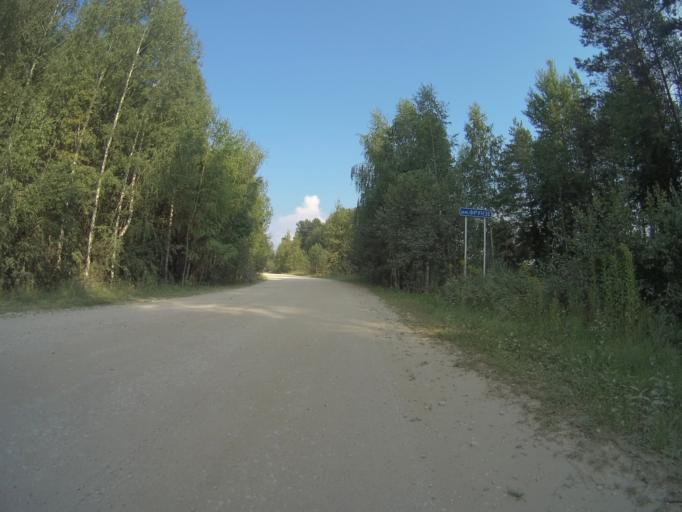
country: RU
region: Vladimir
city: Orgtrud
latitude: 56.3224
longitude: 40.7229
